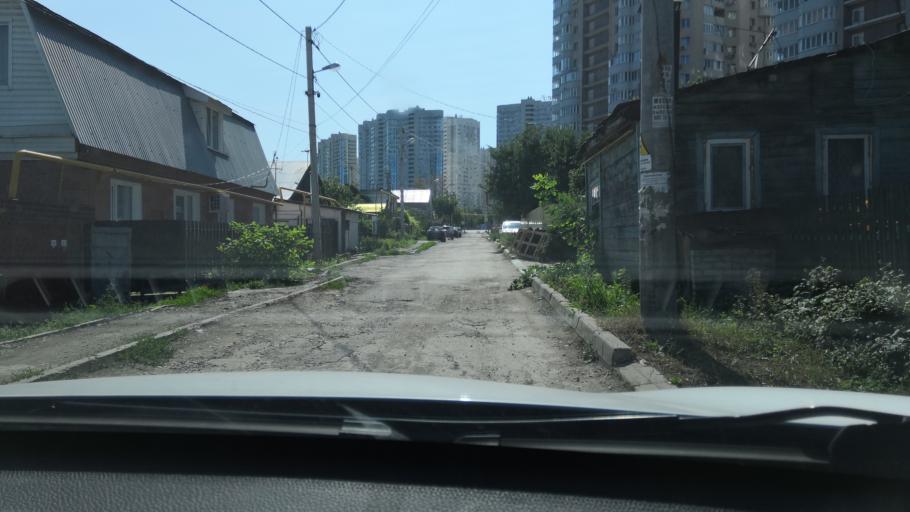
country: RU
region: Samara
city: Samara
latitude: 53.2210
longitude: 50.1611
